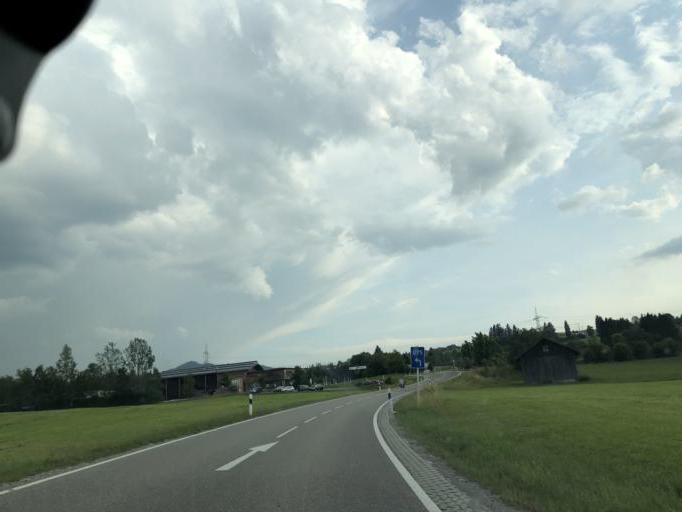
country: DE
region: Bavaria
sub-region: Swabia
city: Oy-Mittelberg
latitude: 47.6575
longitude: 10.4575
